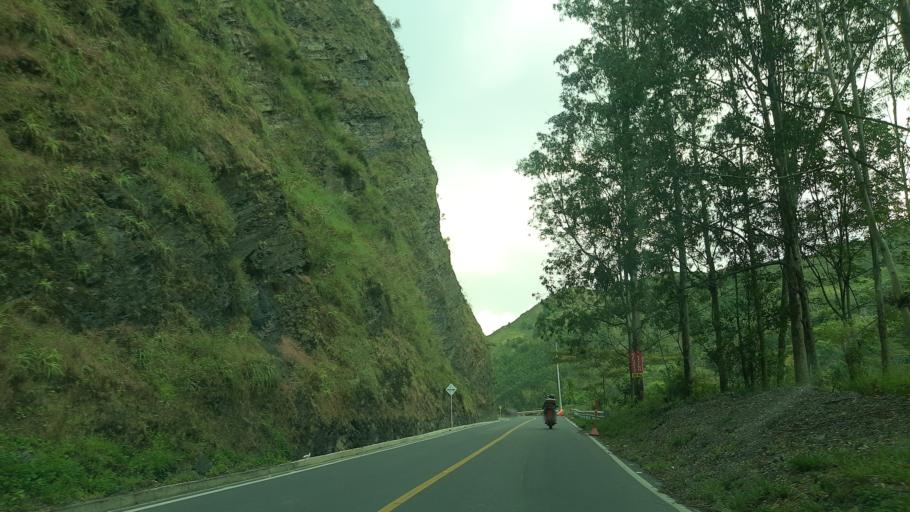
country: CO
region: Boyaca
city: Somondoco
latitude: 5.0107
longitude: -73.3973
